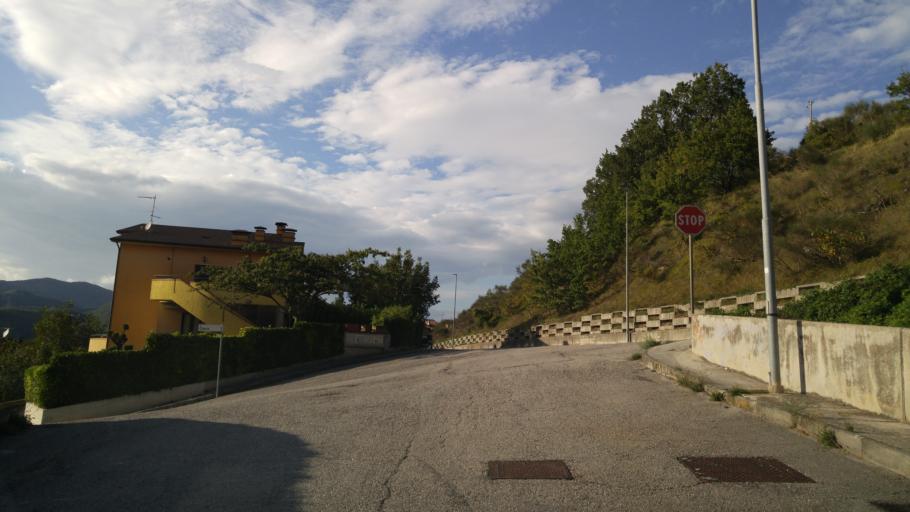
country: IT
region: The Marches
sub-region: Provincia di Pesaro e Urbino
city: Cagli
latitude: 43.5426
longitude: 12.6574
